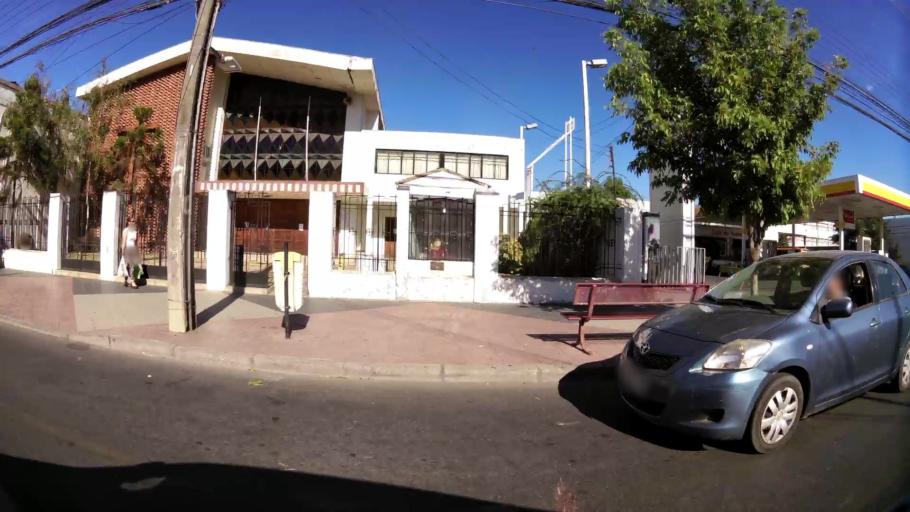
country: CL
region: O'Higgins
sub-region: Provincia de Colchagua
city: Chimbarongo
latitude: -34.5888
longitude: -70.9855
